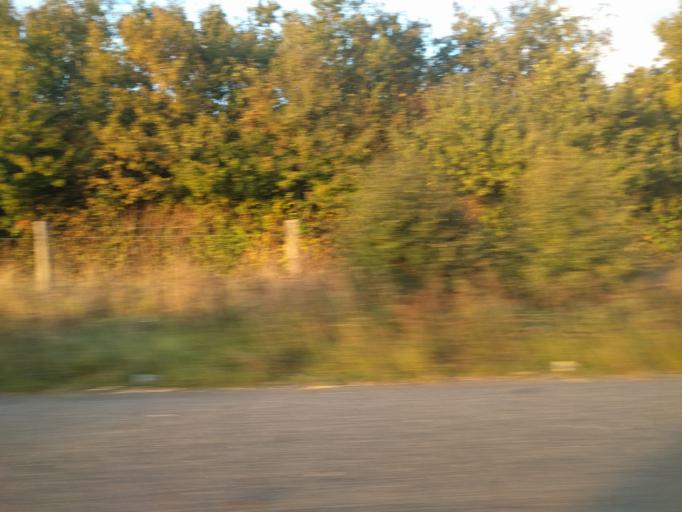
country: DK
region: South Denmark
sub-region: Nyborg Kommune
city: Nyborg
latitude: 55.3377
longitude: 10.7219
